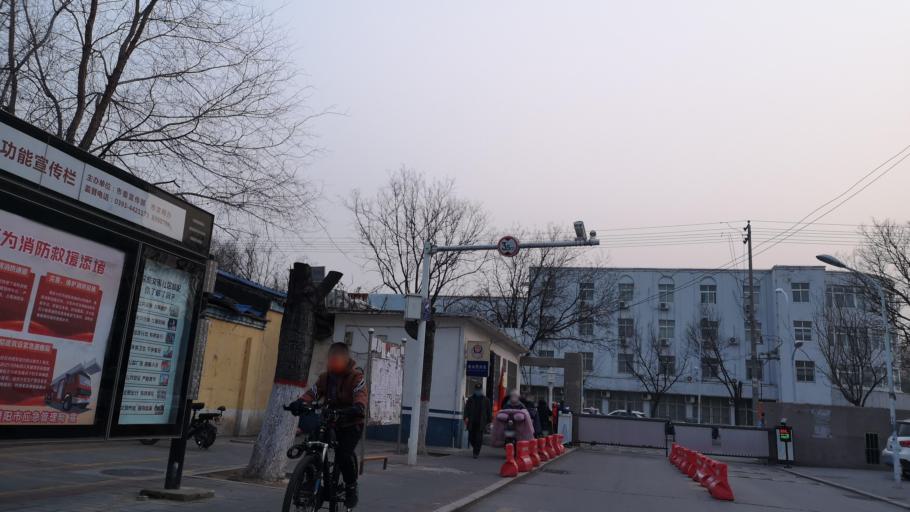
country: CN
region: Henan Sheng
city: Zhongyuanlu
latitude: 35.7806
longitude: 115.0746
